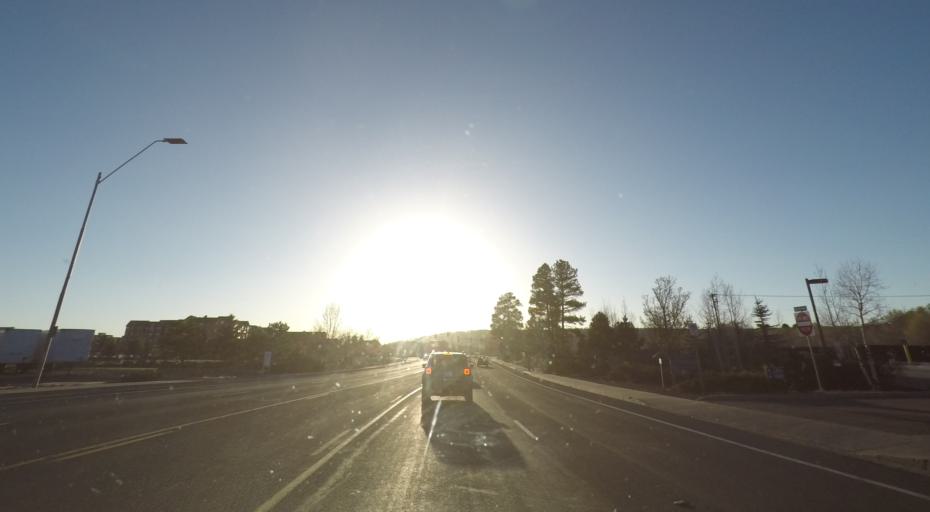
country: US
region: Arizona
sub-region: Coconino County
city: Flagstaff
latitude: 35.1919
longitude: -111.6387
